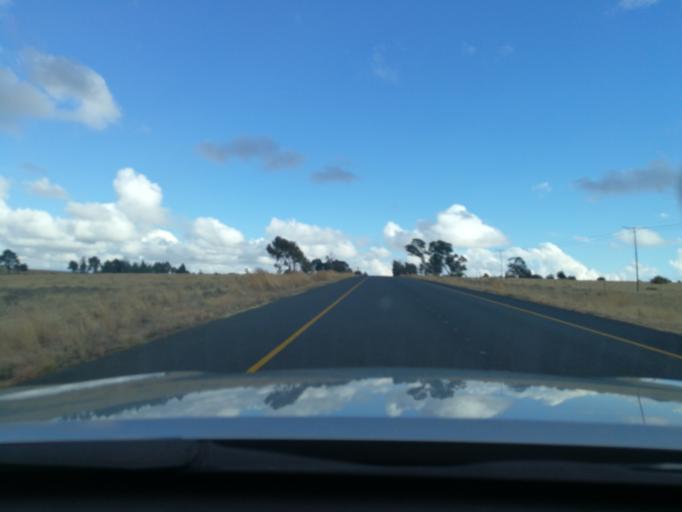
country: ZA
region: Orange Free State
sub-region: Thabo Mofutsanyana District Municipality
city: Reitz
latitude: -27.9176
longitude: 28.3912
